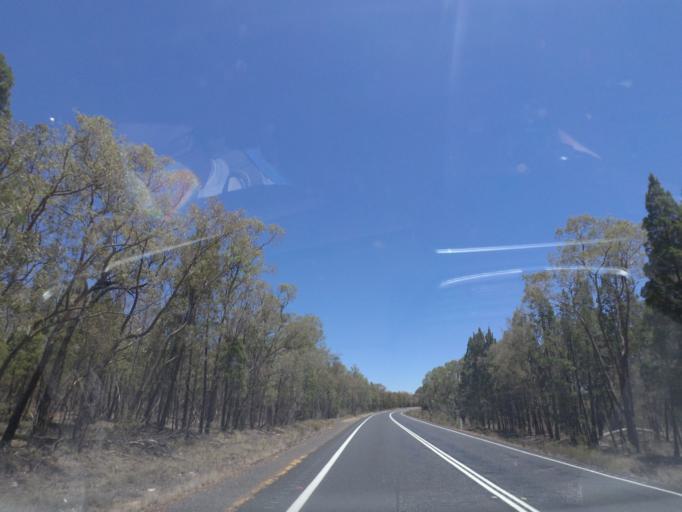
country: AU
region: New South Wales
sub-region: Warrumbungle Shire
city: Coonabarabran
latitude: -31.1950
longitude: 149.3514
